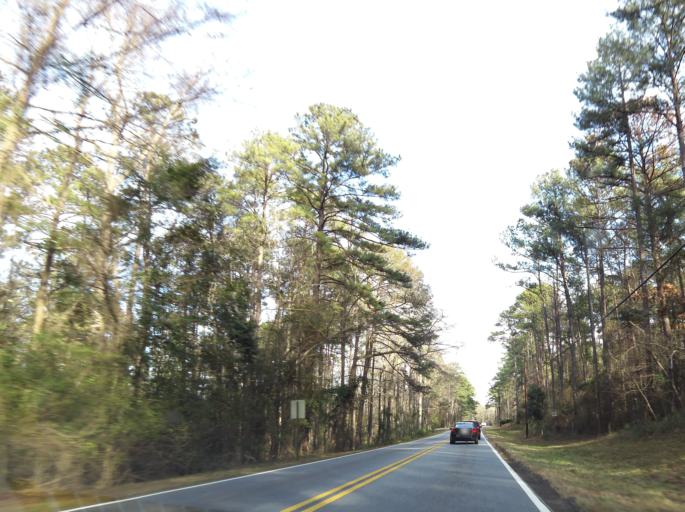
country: US
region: Georgia
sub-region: Bibb County
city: Macon
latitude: 32.8633
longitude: -83.7293
